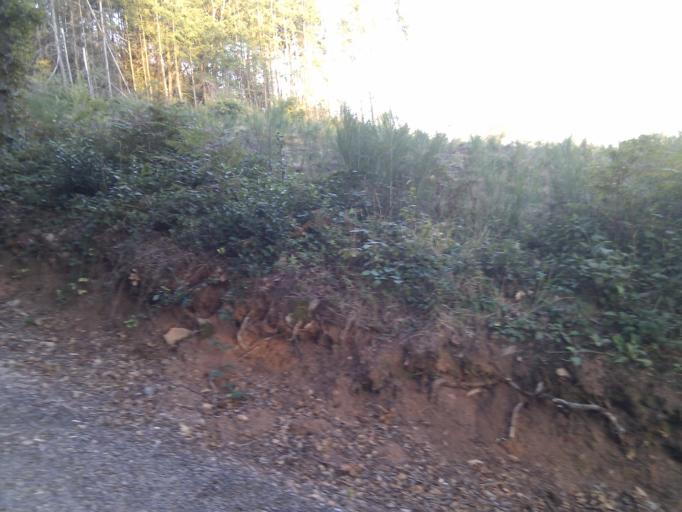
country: FR
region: Bourgogne
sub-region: Departement de la Nievre
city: Lormes
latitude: 47.2919
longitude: 4.0100
